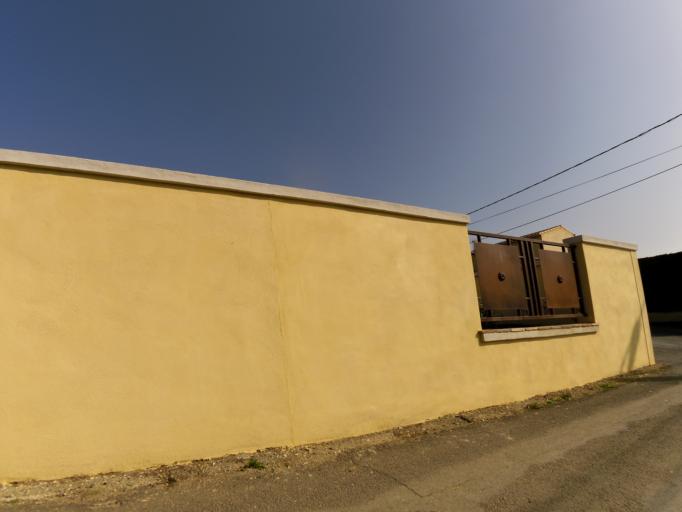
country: FR
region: Languedoc-Roussillon
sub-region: Departement du Gard
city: Beauvoisin
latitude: 43.7160
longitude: 4.3153
